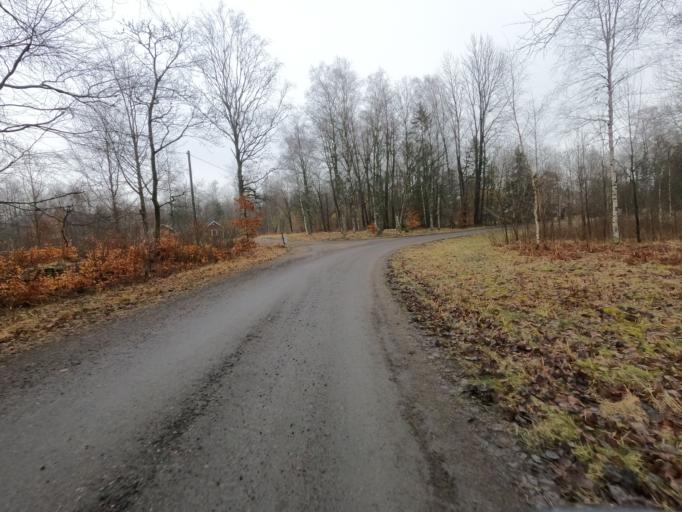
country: SE
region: Halland
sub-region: Hylte Kommun
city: Hyltebruk
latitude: 56.8271
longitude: 13.4201
